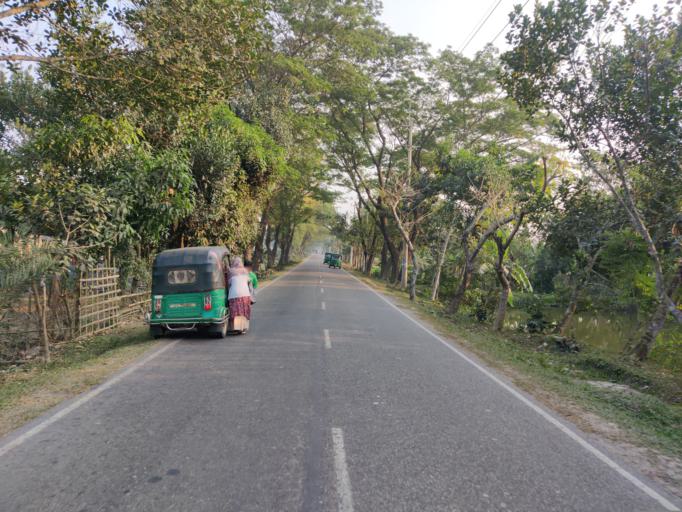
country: BD
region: Dhaka
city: Narsingdi
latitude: 24.0902
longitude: 90.7260
